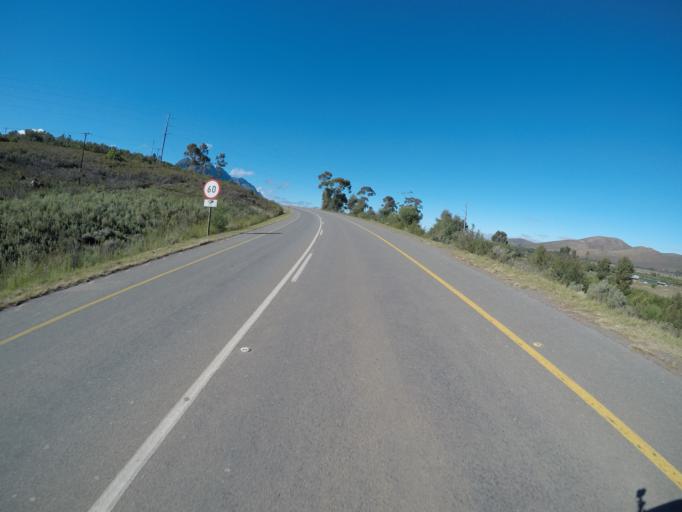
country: ZA
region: Western Cape
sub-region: Overberg District Municipality
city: Caledon
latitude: -34.0559
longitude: 19.5979
